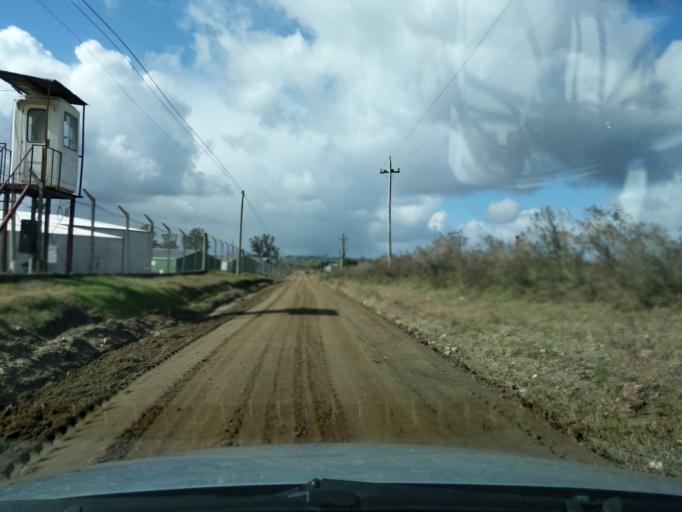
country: UY
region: Florida
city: Florida
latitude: -34.1140
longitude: -56.2311
